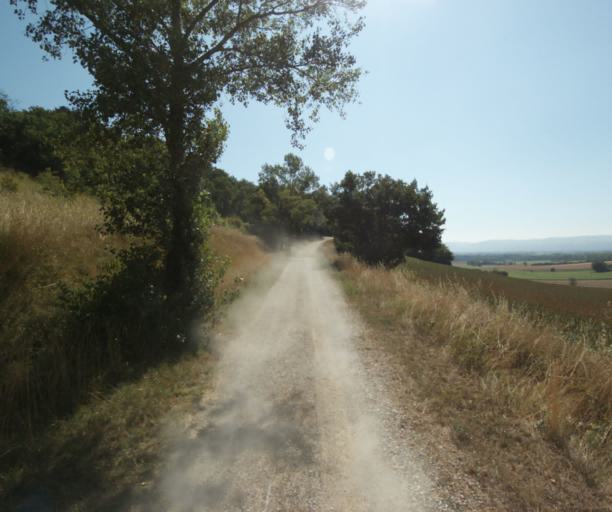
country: FR
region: Midi-Pyrenees
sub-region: Departement de la Haute-Garonne
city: Revel
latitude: 43.5122
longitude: 1.9436
